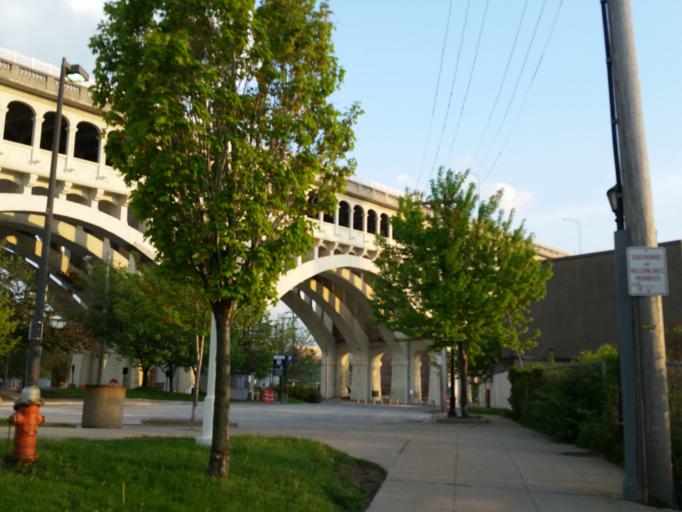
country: US
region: Ohio
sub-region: Cuyahoga County
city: Cleveland
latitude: 41.4963
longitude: -81.7010
